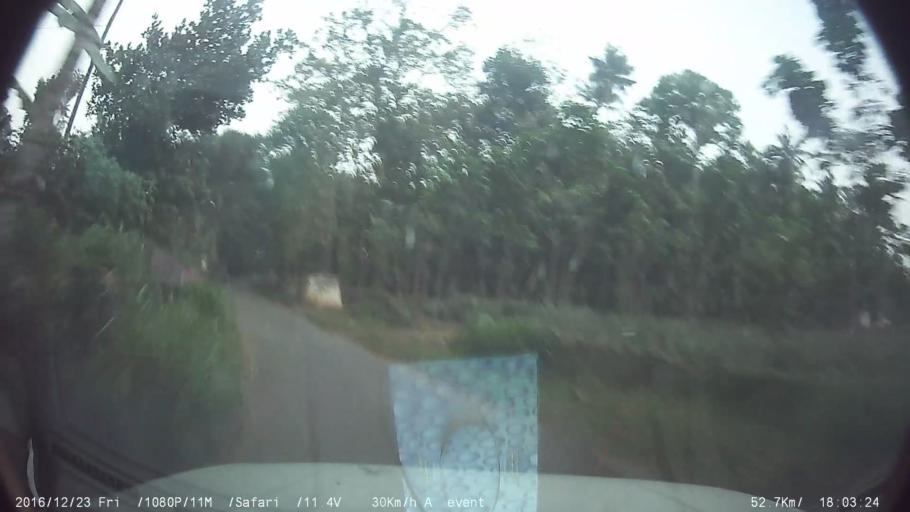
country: IN
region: Kerala
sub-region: Kottayam
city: Palackattumala
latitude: 9.7784
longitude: 76.5871
